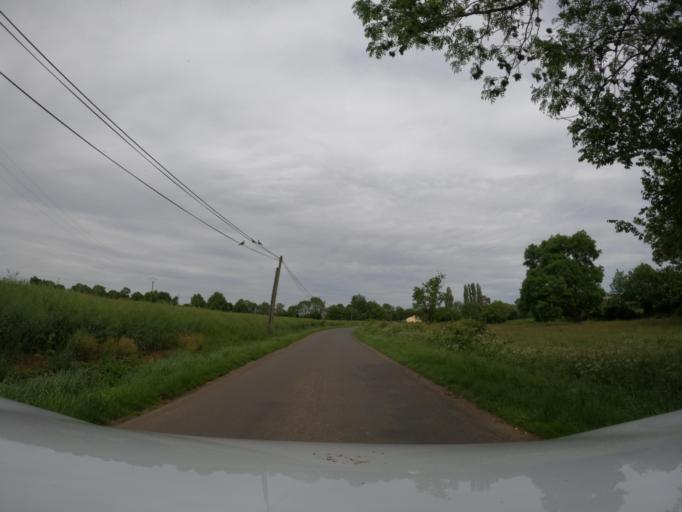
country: FR
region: Pays de la Loire
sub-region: Departement de la Vendee
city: Saint-Hilaire-des-Loges
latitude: 46.4793
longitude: -0.6525
